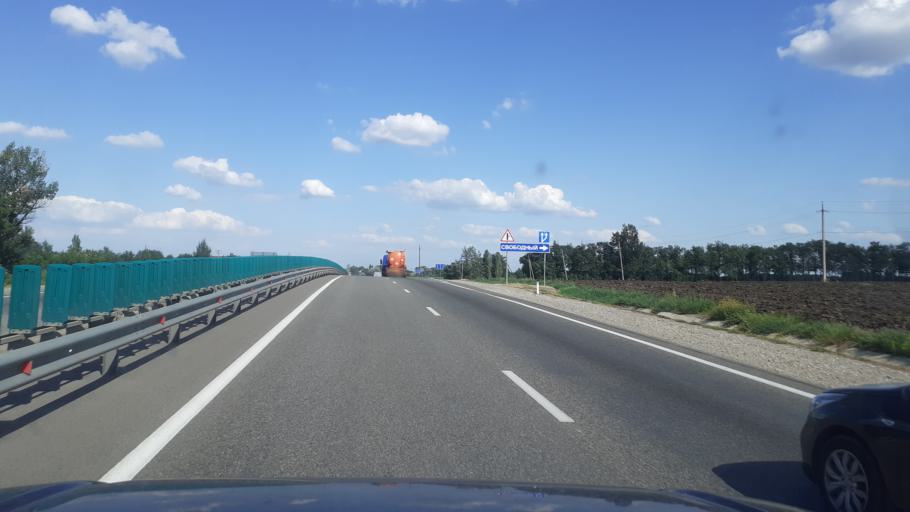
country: RU
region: Krasnodarskiy
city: Severskaya
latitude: 44.8545
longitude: 38.7155
